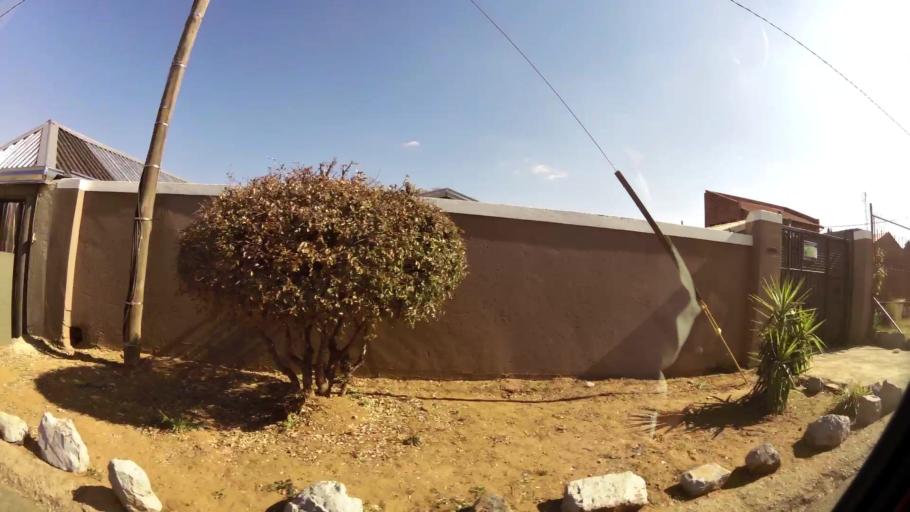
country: ZA
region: Gauteng
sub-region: City of Johannesburg Metropolitan Municipality
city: Soweto
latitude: -26.2422
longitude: 27.8988
